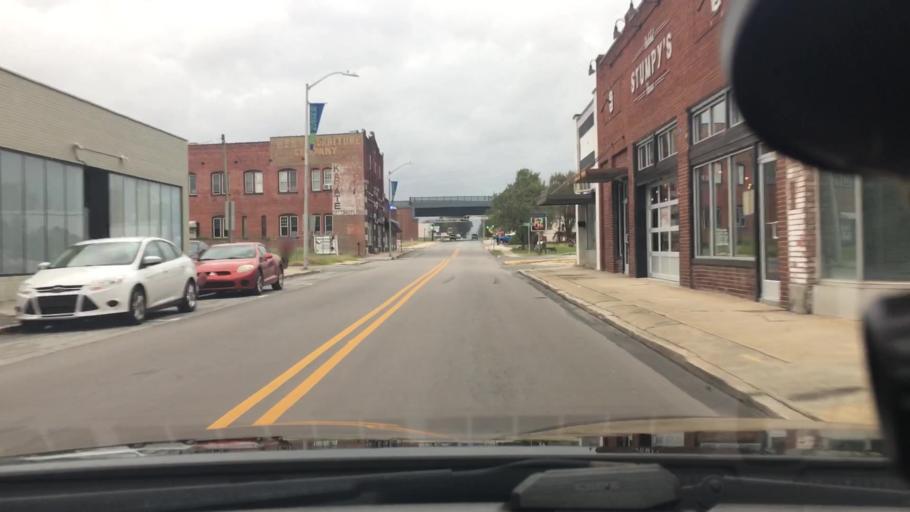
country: US
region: North Carolina
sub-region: Pitt County
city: Greenville
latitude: 35.6087
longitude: -77.3776
